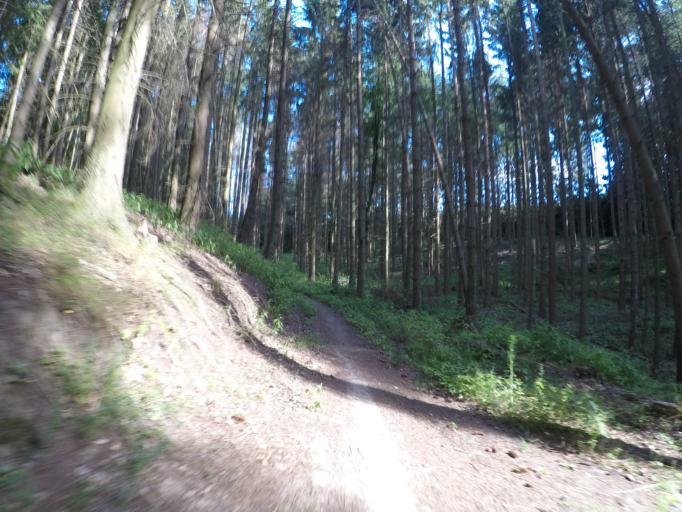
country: LU
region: Luxembourg
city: Itzig
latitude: 49.6004
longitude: 6.1689
